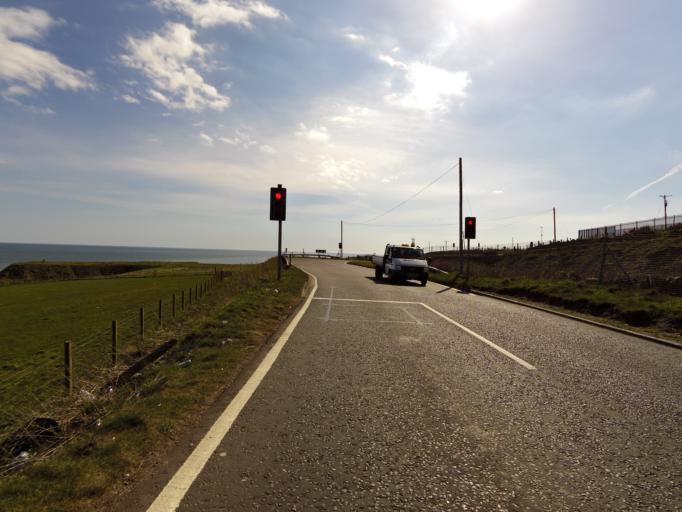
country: GB
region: Scotland
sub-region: Aberdeen City
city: Aberdeen
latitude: 57.1260
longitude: -2.0541
